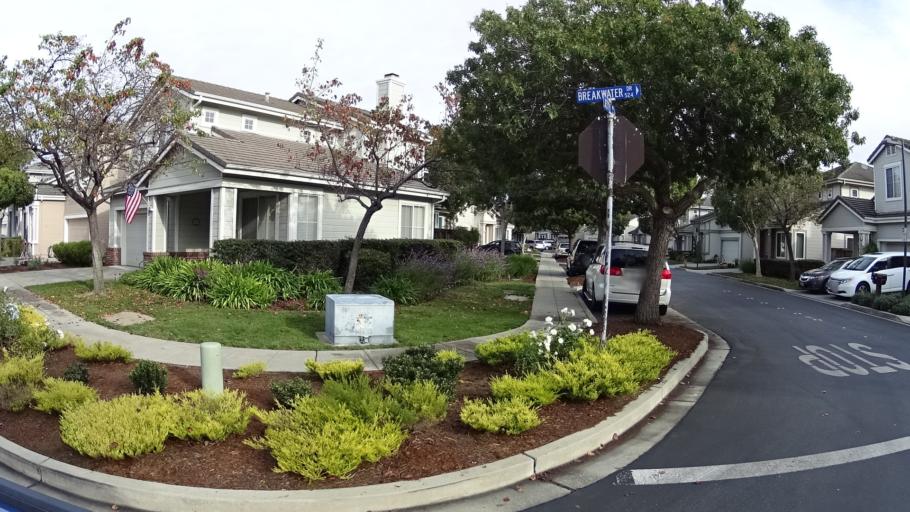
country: US
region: California
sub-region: San Mateo County
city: Redwood Shores
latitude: 37.5392
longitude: -122.2383
